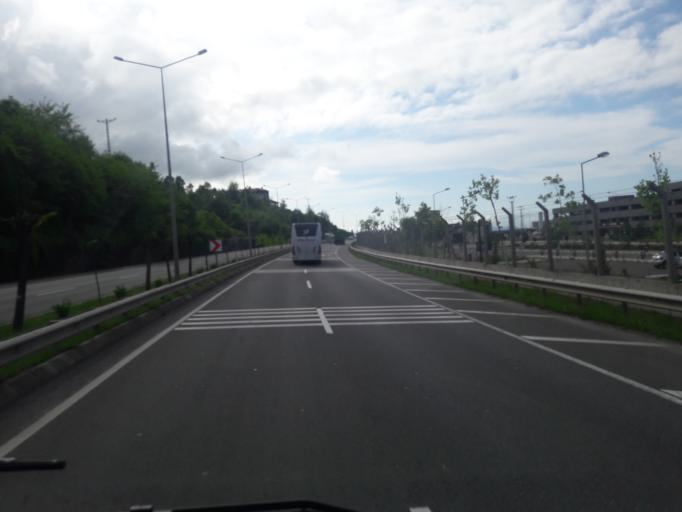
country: TR
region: Ordu
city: Gulyali
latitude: 40.9630
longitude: 38.0795
